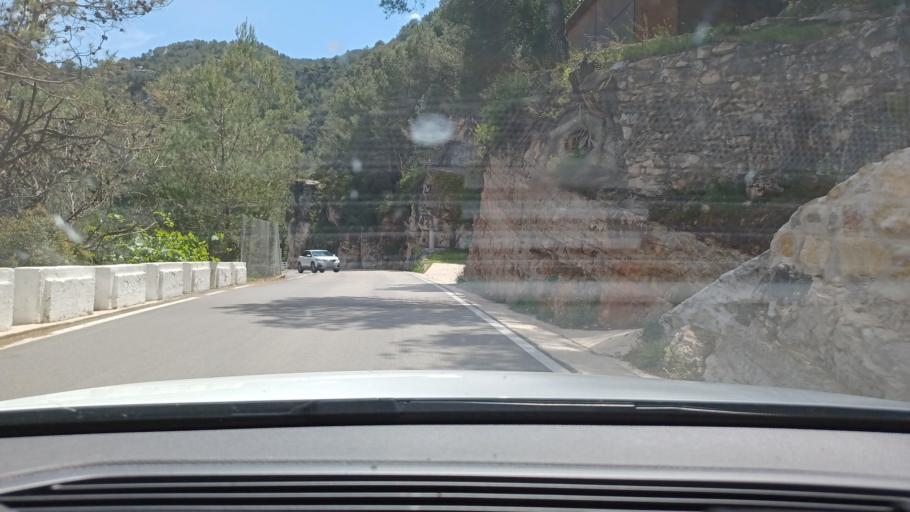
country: ES
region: Valencia
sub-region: Provincia de Castello
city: Rosell
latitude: 40.6711
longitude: 0.2327
